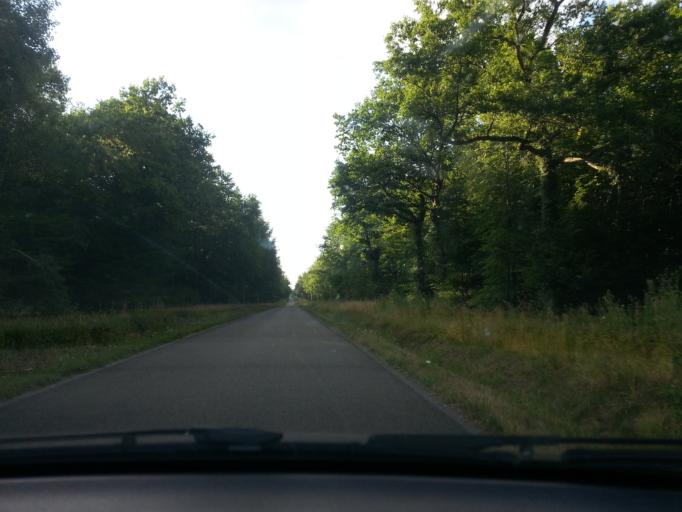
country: FR
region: Bourgogne
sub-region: Departement de Saone-et-Loire
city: Dracy-le-Fort
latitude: 46.7640
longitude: 4.7732
